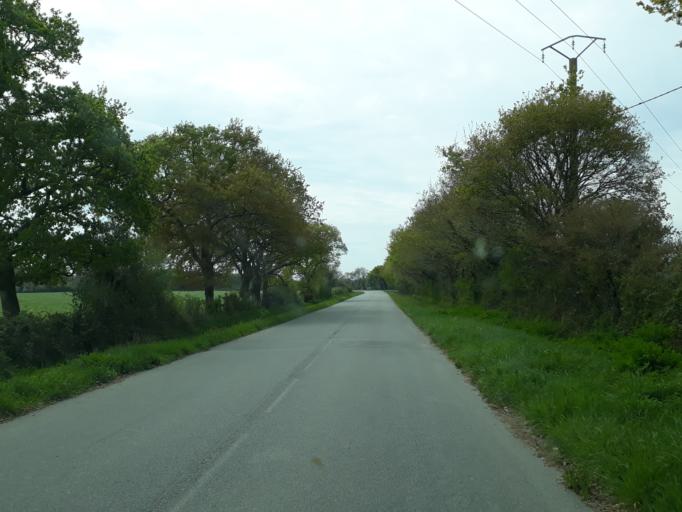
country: FR
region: Pays de la Loire
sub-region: Departement de la Loire-Atlantique
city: Saint-Molf
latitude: 47.3704
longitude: -2.4086
